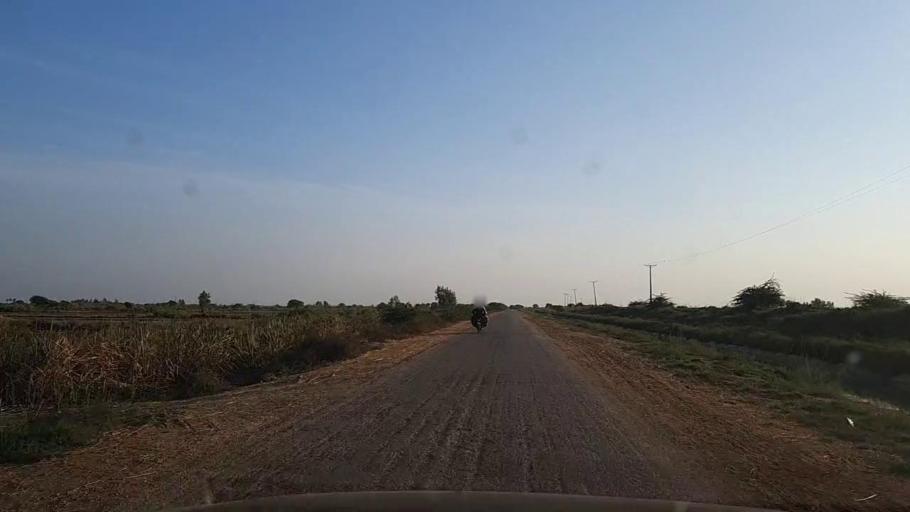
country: PK
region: Sindh
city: Thatta
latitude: 24.6413
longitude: 67.9125
